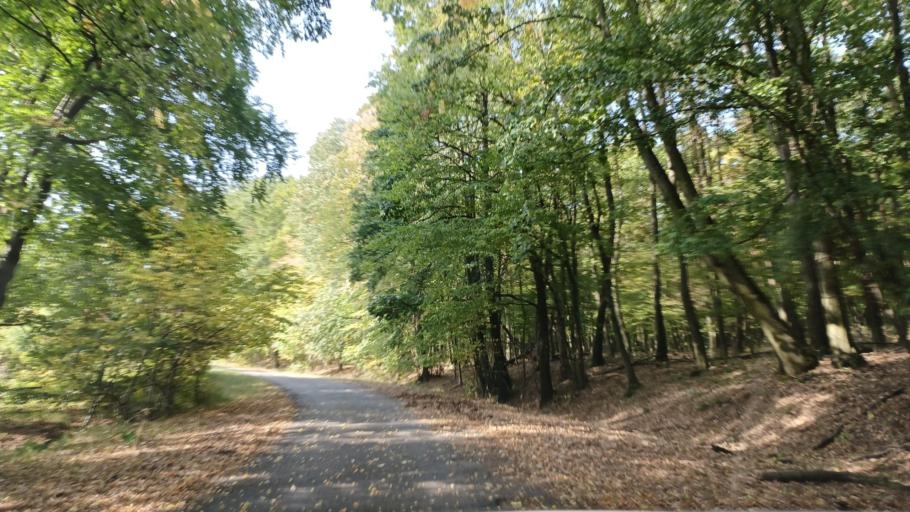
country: HU
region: Baranya
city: Mecseknadasd
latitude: 46.1996
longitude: 18.4530
